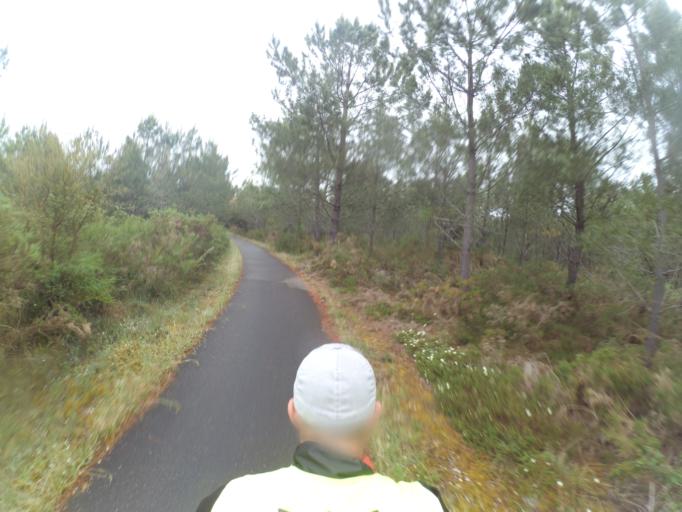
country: FR
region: Aquitaine
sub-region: Departement des Landes
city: Mimizan
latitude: 44.2244
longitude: -1.2604
